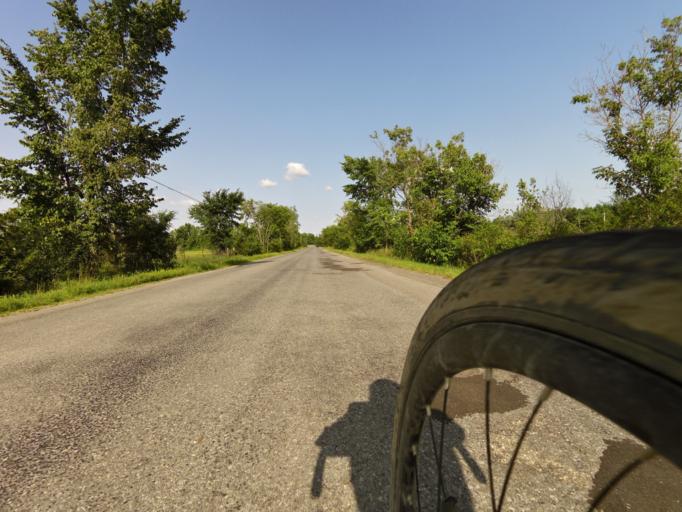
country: CA
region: Ontario
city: Kingston
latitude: 44.3485
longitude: -76.6468
